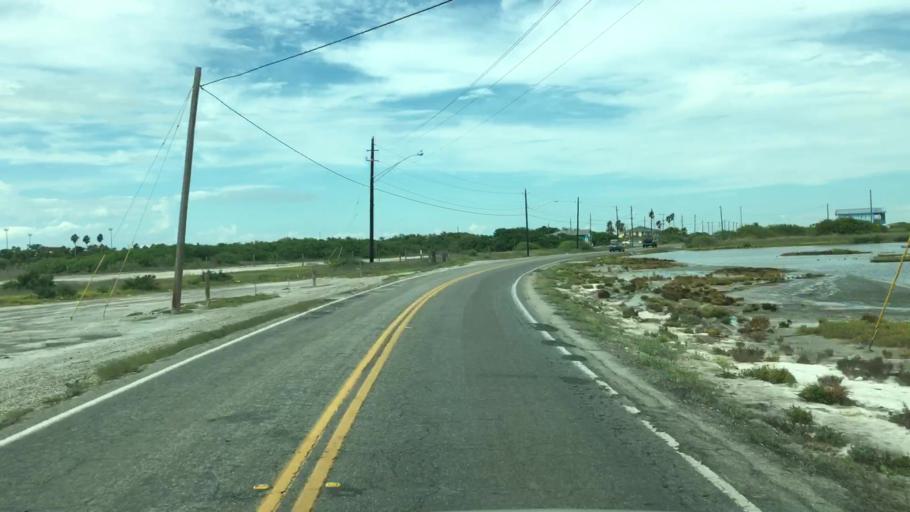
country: US
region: Texas
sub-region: Nueces County
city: Corpus Christi
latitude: 27.6386
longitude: -97.2875
